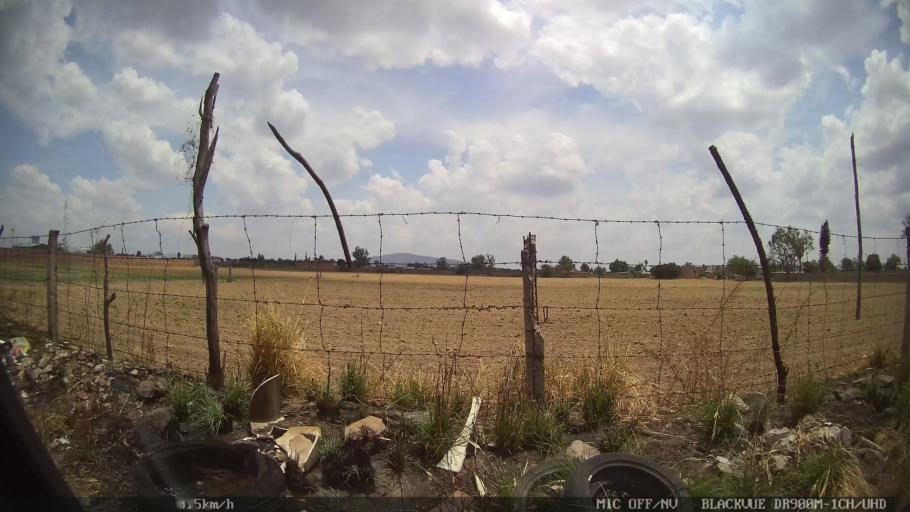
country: MX
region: Jalisco
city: Tonala
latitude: 20.6658
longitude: -103.2305
